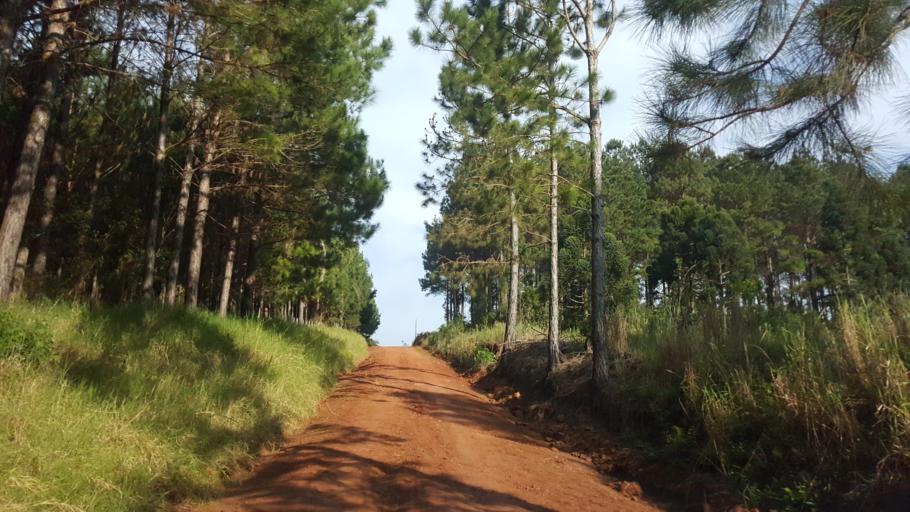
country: AR
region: Misiones
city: Capiovi
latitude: -26.8938
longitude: -55.0973
